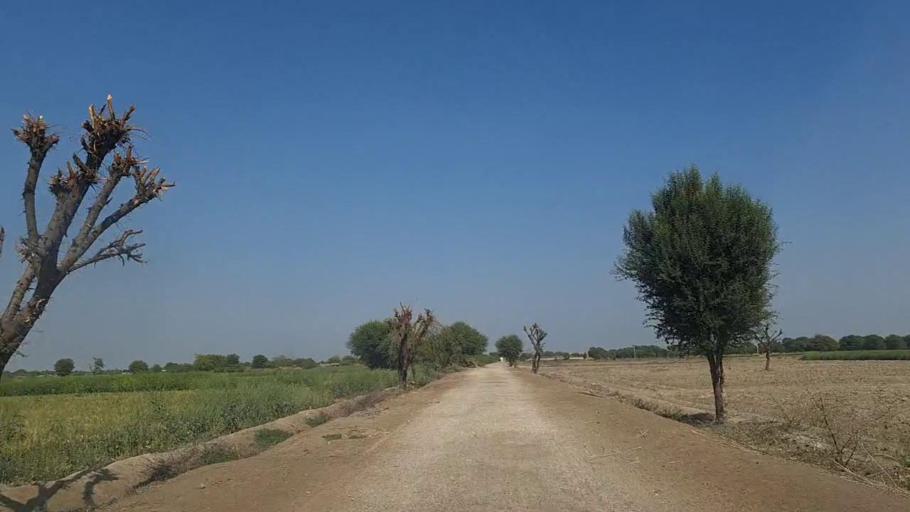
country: PK
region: Sindh
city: Digri
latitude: 25.1677
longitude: 69.1356
